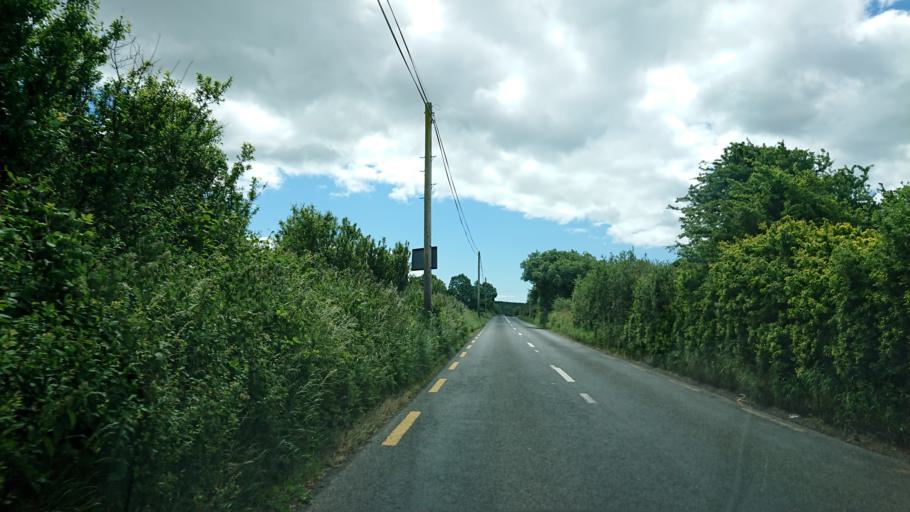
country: IE
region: Munster
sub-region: Waterford
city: Tra Mhor
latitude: 52.1930
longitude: -7.1856
